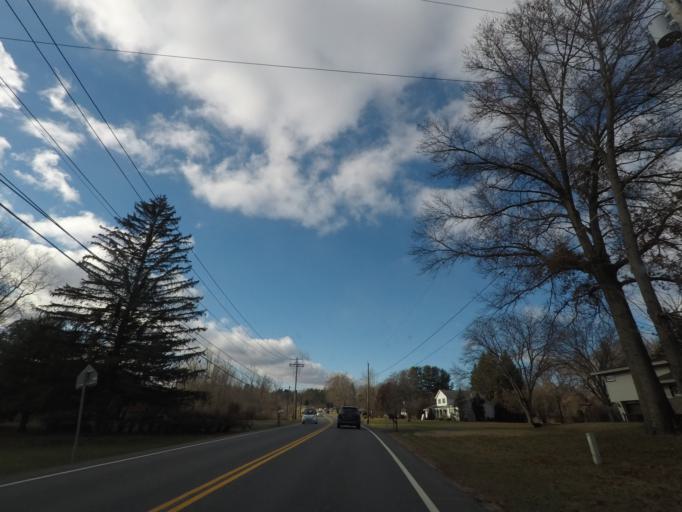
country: US
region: New York
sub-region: Schenectady County
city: East Glenville
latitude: 42.8676
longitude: -73.9183
